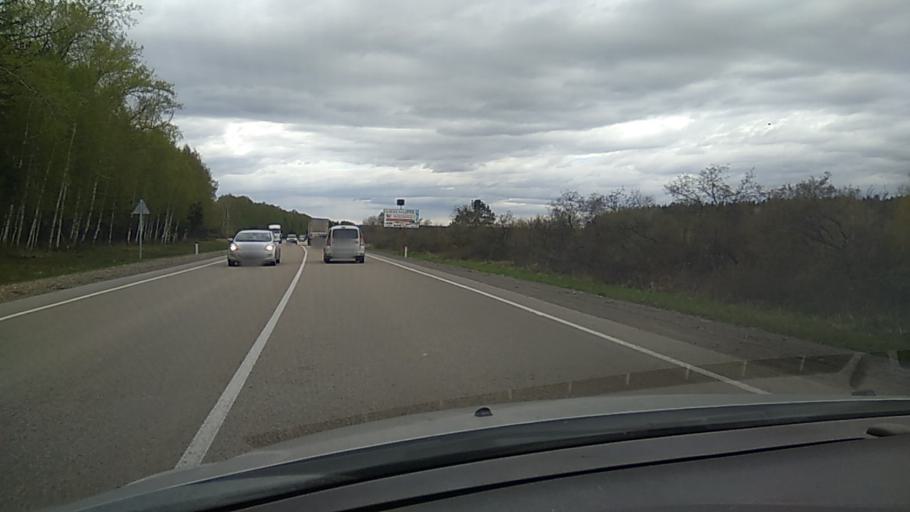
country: RU
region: Sverdlovsk
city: Dvurechensk
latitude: 56.6737
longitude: 61.1415
